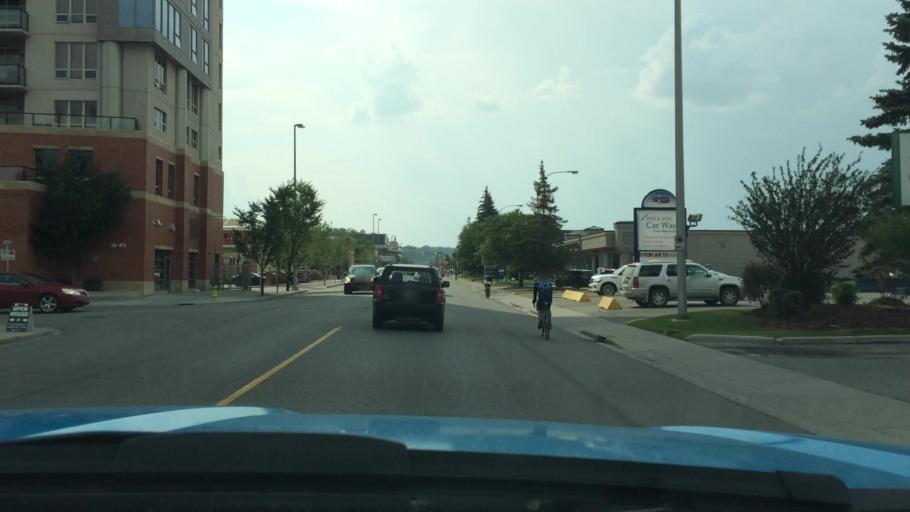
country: CA
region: Alberta
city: Calgary
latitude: 51.0440
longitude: -114.0859
